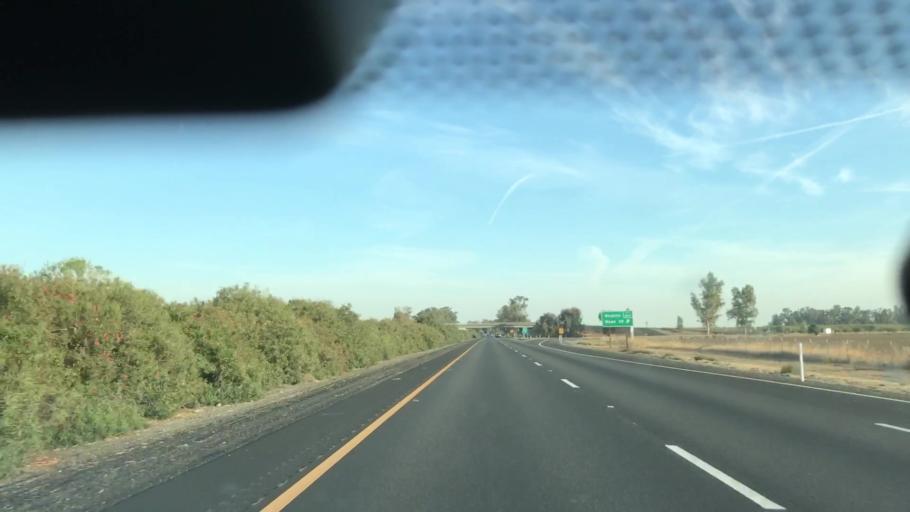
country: US
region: California
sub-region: Glenn County
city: Willows
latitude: 39.5784
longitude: -122.2109
